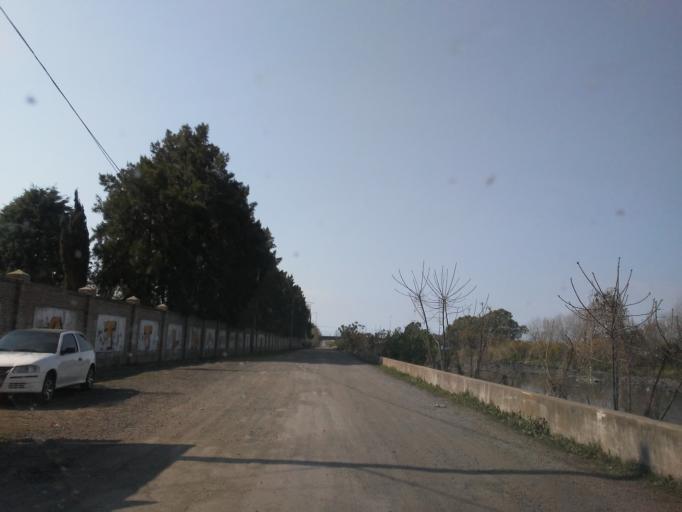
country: AR
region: Buenos Aires
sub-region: Partido de Avellaneda
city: Avellaneda
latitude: -34.6838
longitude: -58.3193
